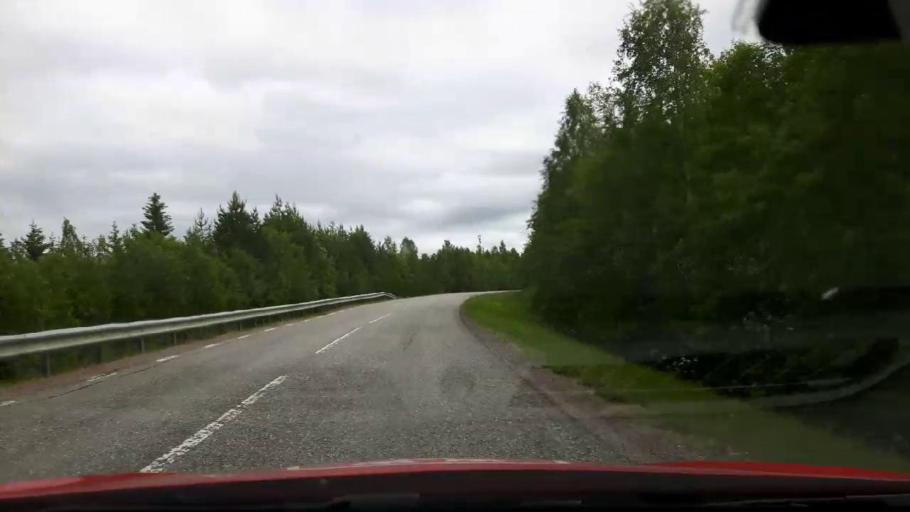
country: SE
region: Jaemtland
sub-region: Ragunda Kommun
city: Hammarstrand
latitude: 63.0414
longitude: 16.3907
